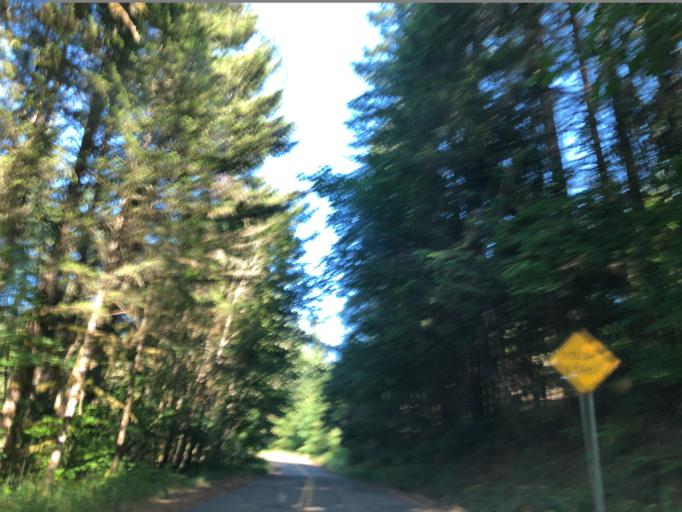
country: US
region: Oregon
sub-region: Linn County
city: Sweet Home
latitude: 44.4649
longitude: -122.6743
